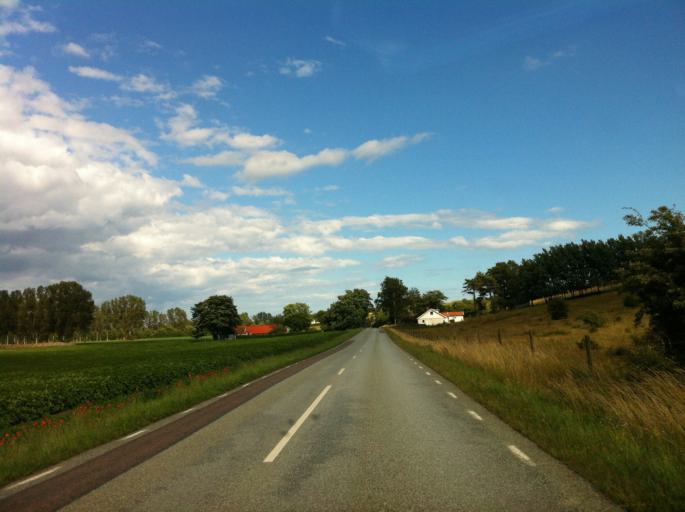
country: SE
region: Skane
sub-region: Ystads Kommun
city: Kopingebro
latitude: 55.4045
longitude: 14.0229
